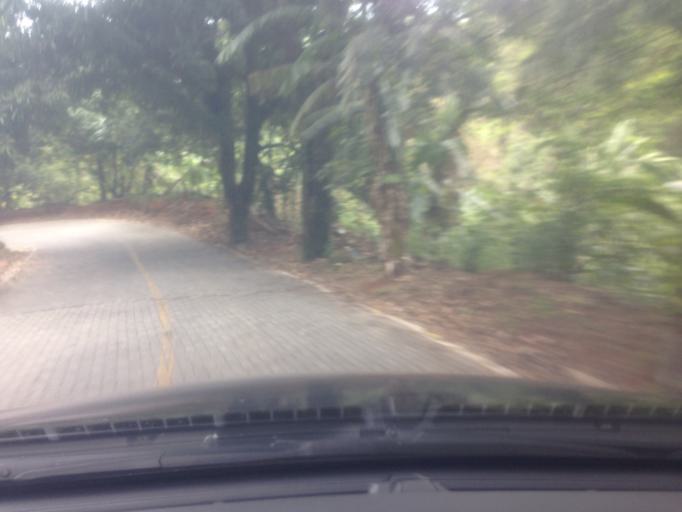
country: BR
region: Espirito Santo
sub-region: Guarapari
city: Guarapari
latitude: -20.6166
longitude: -40.5327
